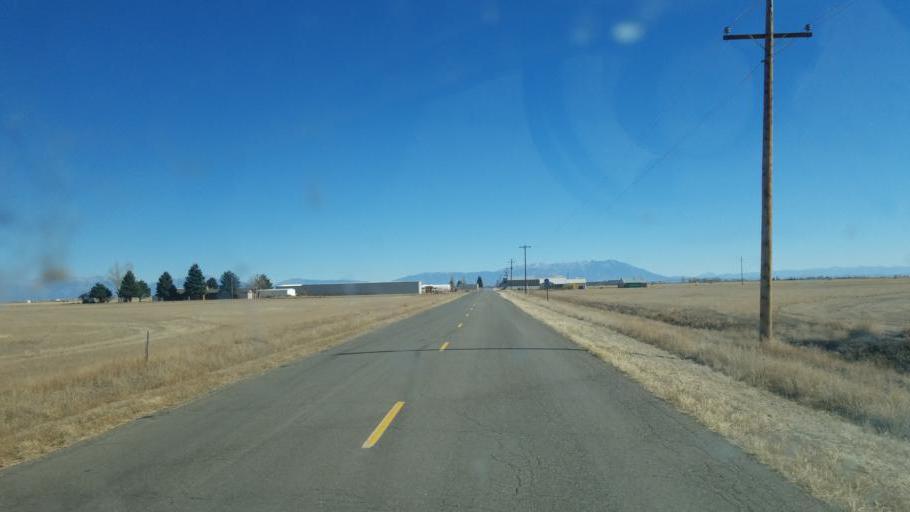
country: US
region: Colorado
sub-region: Rio Grande County
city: Monte Vista
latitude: 37.6474
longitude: -106.1146
